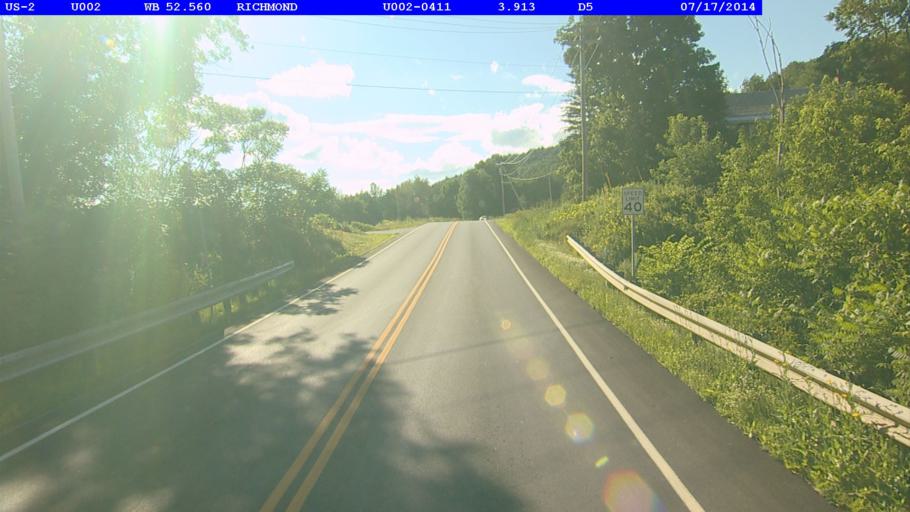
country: US
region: Vermont
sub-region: Chittenden County
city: Williston
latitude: 44.4006
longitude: -72.9737
